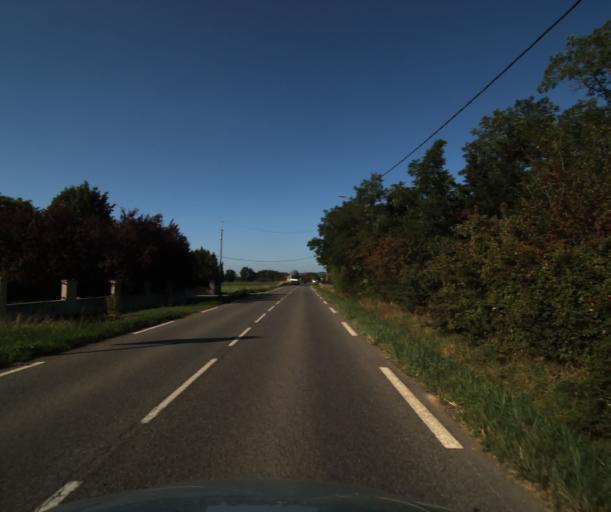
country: FR
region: Midi-Pyrenees
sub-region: Departement de la Haute-Garonne
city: Labarthe-sur-Leze
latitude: 43.4476
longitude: 1.3866
